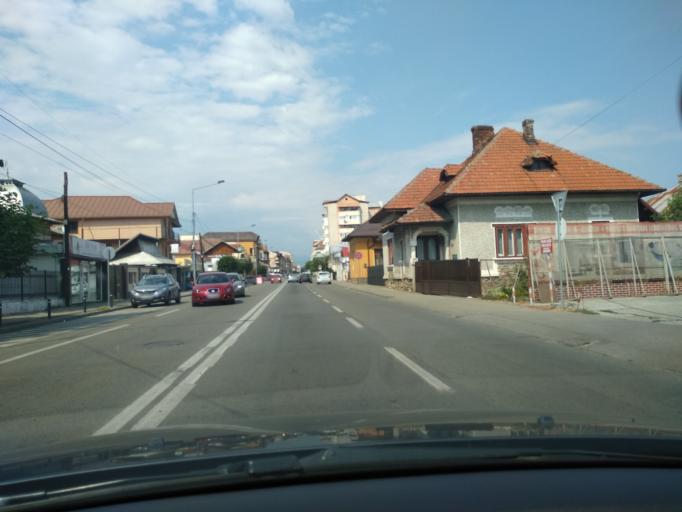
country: RO
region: Gorj
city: Targu Jiu
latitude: 45.0314
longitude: 23.2696
